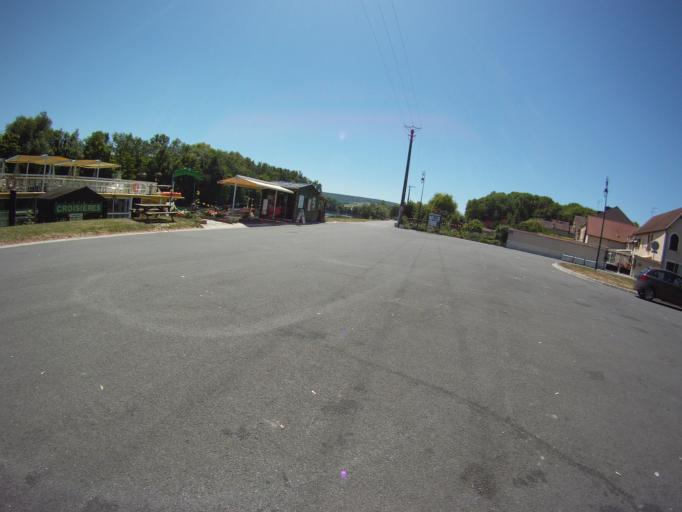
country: FR
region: Champagne-Ardenne
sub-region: Departement de la Marne
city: Mardeuil
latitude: 49.0700
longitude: 3.9248
